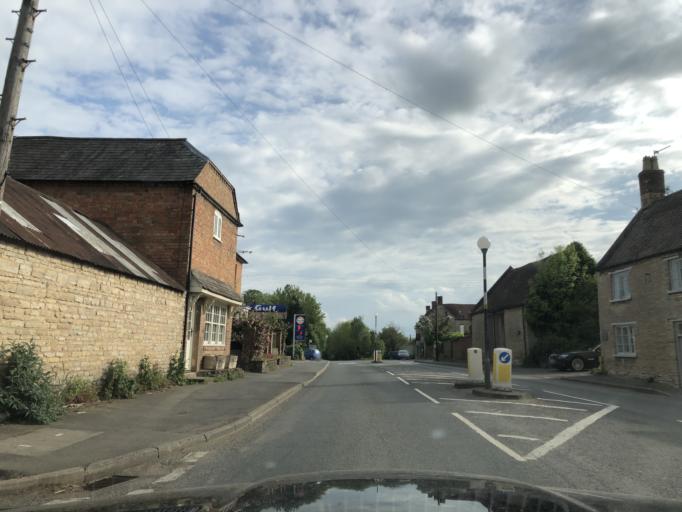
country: GB
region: England
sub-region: Warwickshire
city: Shipston on Stour
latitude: 52.1082
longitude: -1.6212
